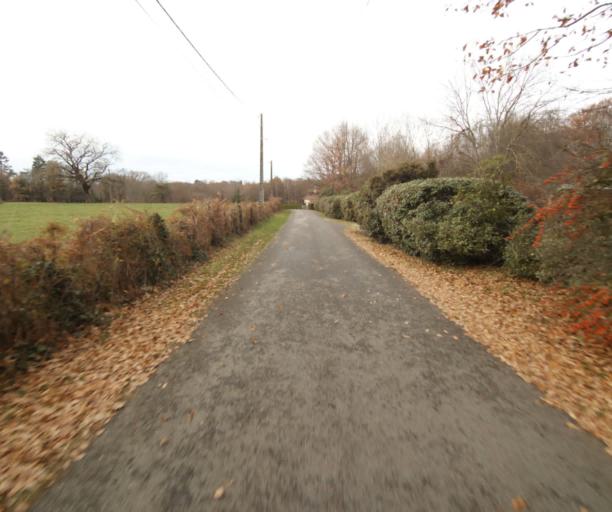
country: FR
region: Limousin
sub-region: Departement de la Correze
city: Chameyrat
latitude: 45.2467
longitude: 1.6673
